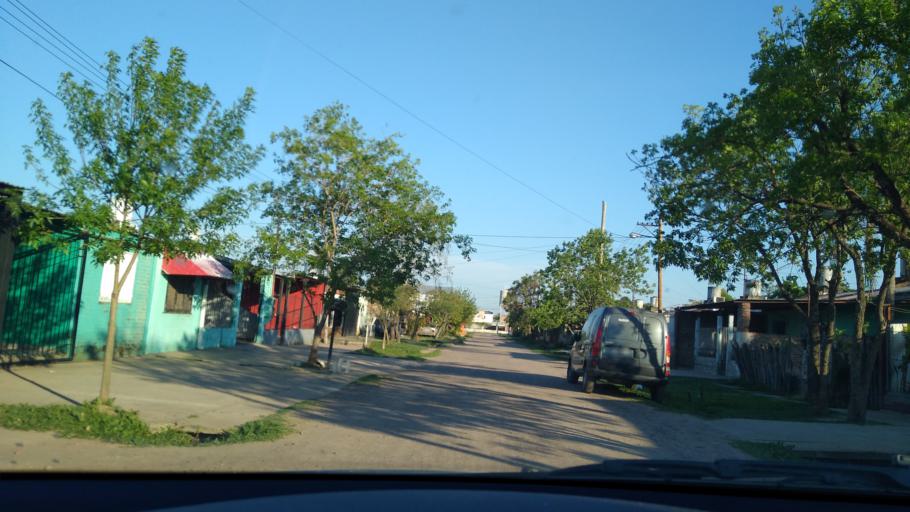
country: AR
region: Chaco
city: Puerto Vilelas
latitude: -27.5121
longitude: -58.9456
